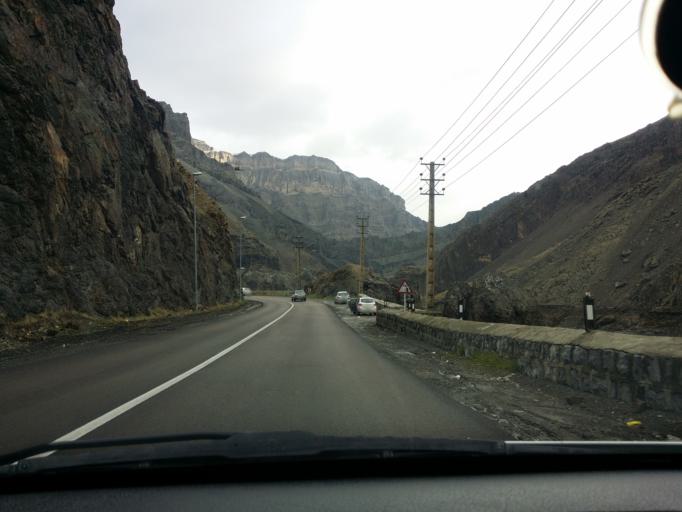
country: IR
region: Alborz
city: Karaj
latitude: 35.9984
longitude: 51.1132
